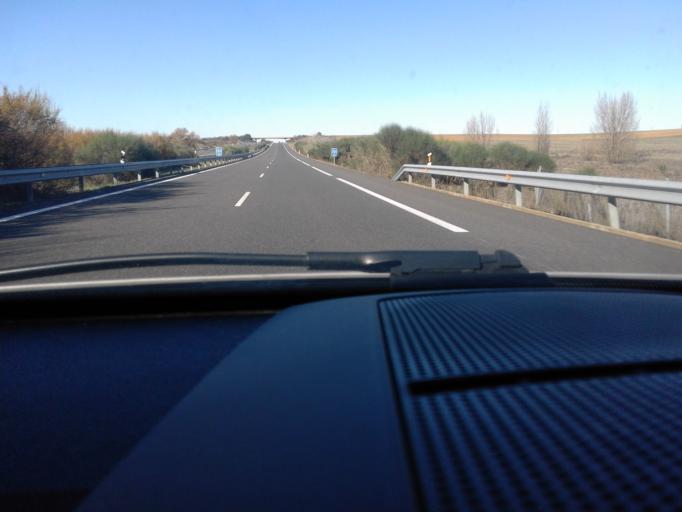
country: ES
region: Castille and Leon
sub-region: Provincia de Leon
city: Villamoratiel de las Matas
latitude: 42.4243
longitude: -5.2895
